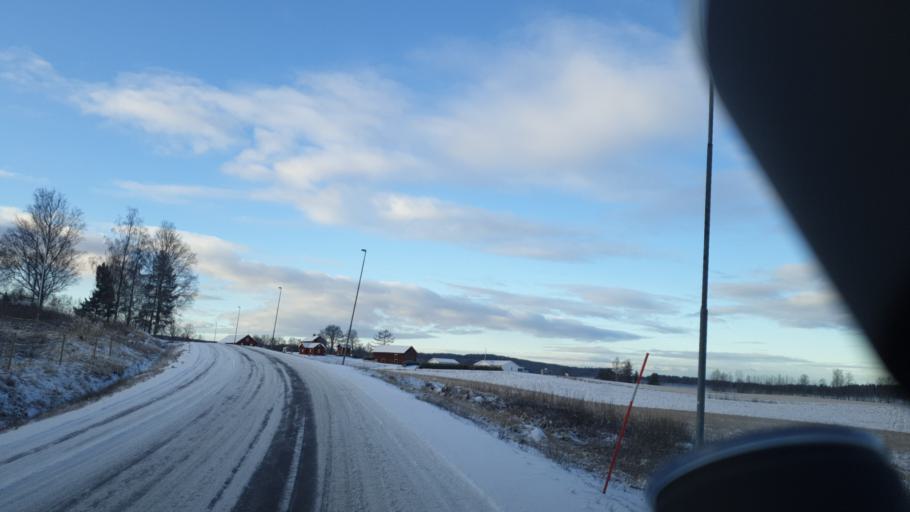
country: SE
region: Vaermland
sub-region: Arvika Kommun
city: Arvika
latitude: 59.7808
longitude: 12.6175
